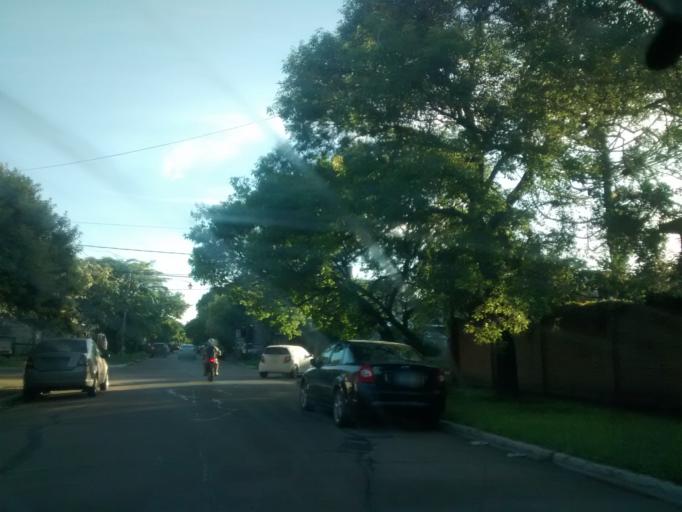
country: AR
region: Chaco
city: Resistencia
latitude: -27.4639
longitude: -58.9744
